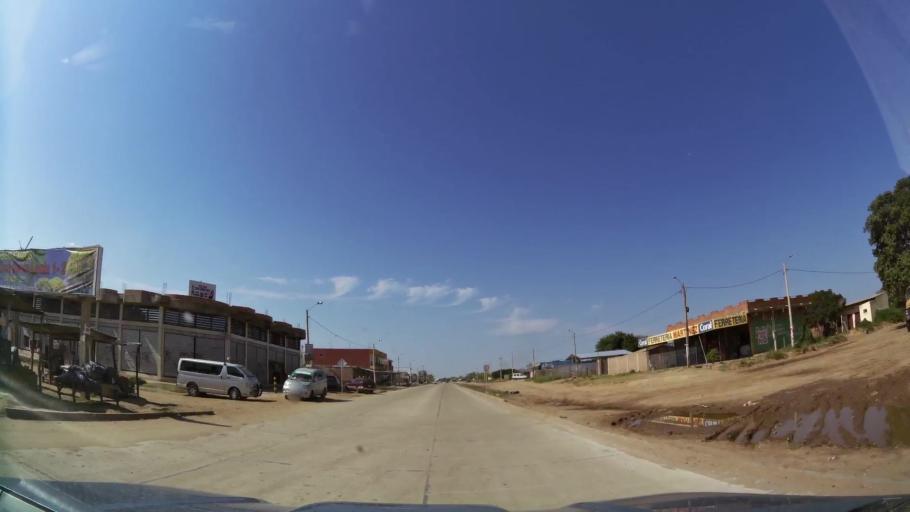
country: BO
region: Santa Cruz
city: Cotoca
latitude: -17.7229
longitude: -63.0795
